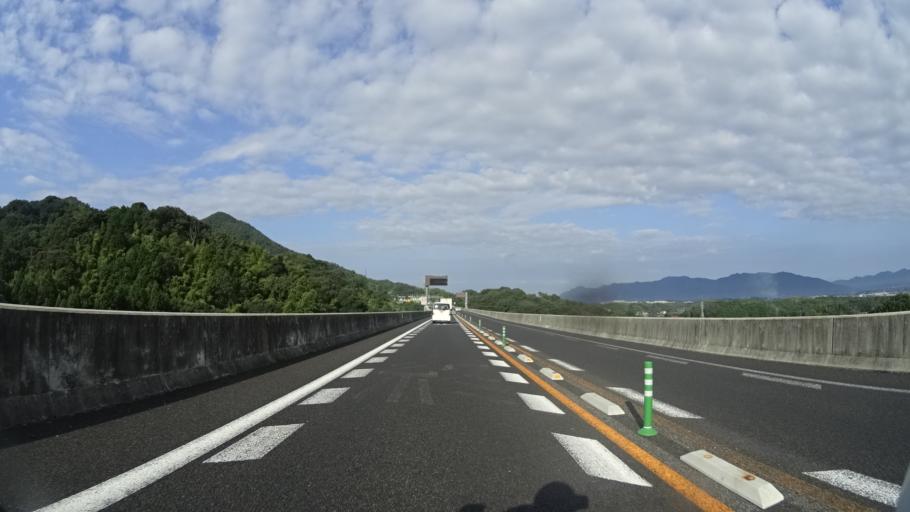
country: JP
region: Shimane
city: Hiratacho
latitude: 35.3684
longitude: 132.8485
